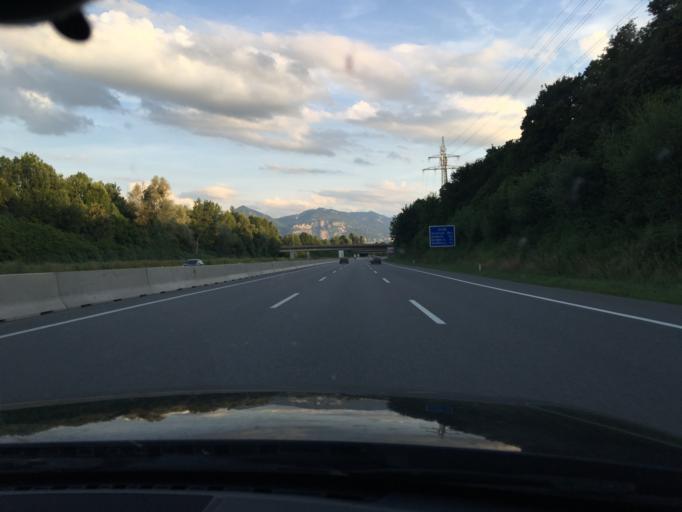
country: AT
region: Vorarlberg
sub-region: Politischer Bezirk Bregenz
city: Lauterach
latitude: 47.4757
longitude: 9.7400
